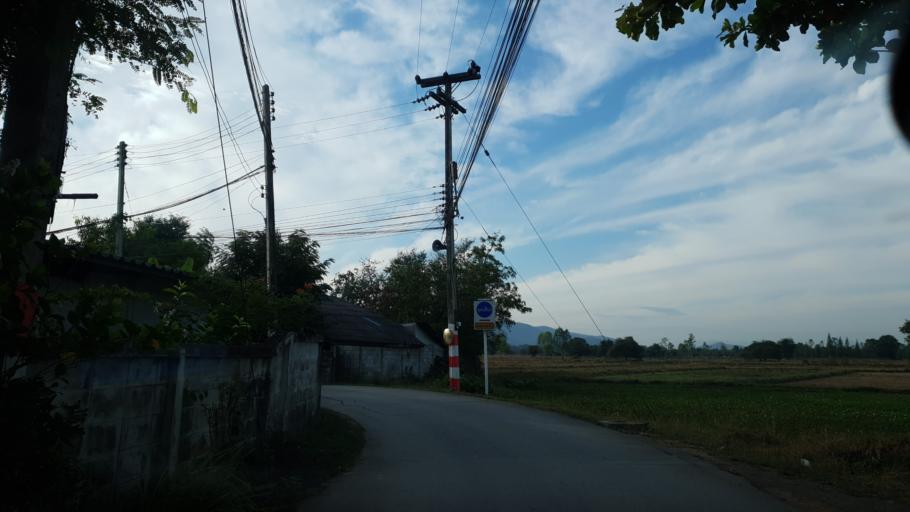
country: TH
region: Lamphun
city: Lamphun
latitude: 18.5222
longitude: 99.0181
